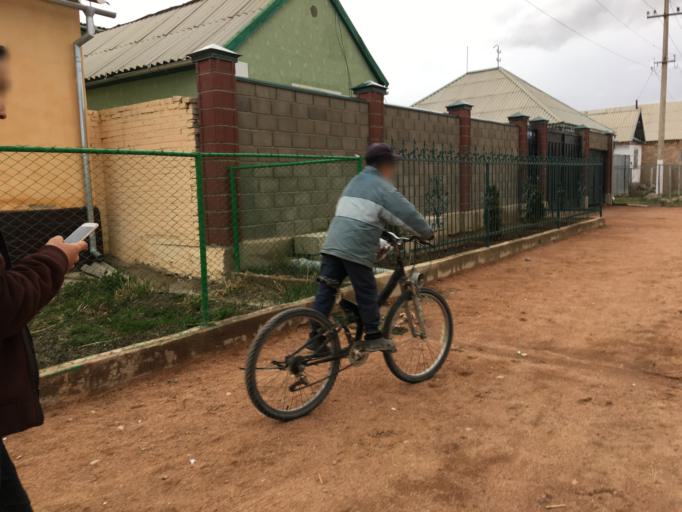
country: KG
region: Ysyk-Koel
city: Bokombayevskoye
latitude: 42.1084
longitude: 76.9795
